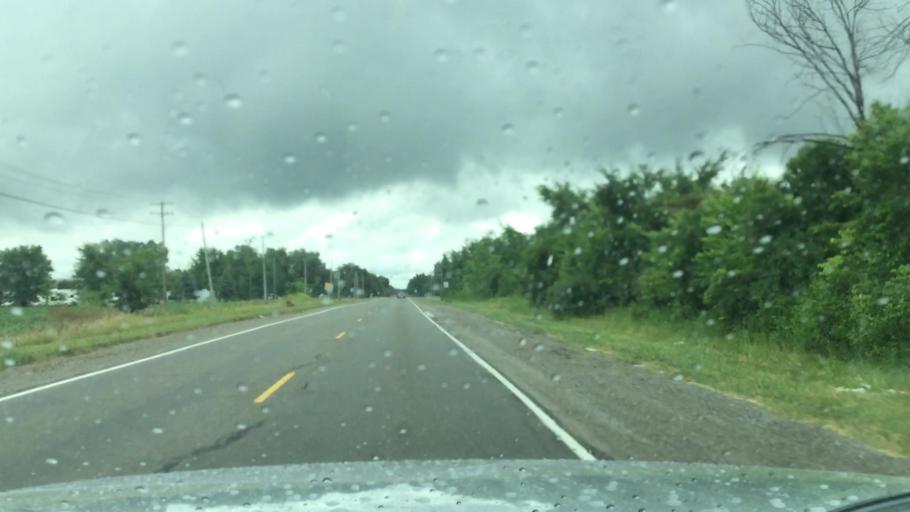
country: US
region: Michigan
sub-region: Genesee County
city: Flushing
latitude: 43.0705
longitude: -83.7732
